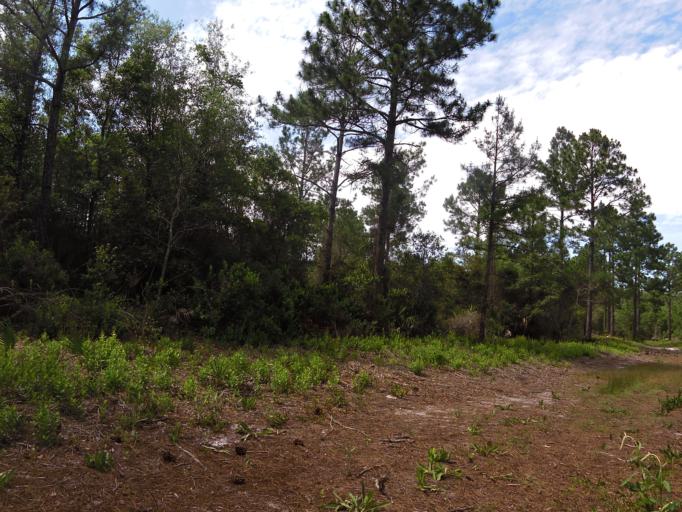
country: US
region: Florida
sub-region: Duval County
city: Atlantic Beach
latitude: 30.4498
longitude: -81.4714
